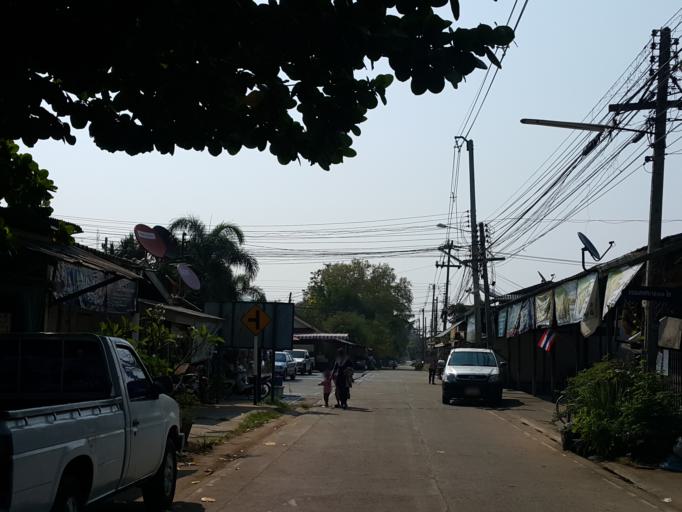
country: TH
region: Kanchanaburi
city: Sai Yok
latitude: 14.1196
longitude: 99.1385
